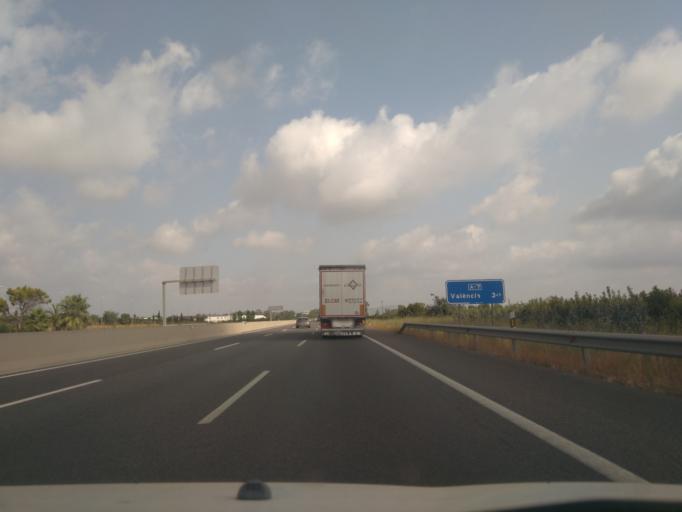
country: ES
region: Valencia
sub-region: Provincia de Valencia
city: L'Alcudia
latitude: 39.2005
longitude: -0.4951
